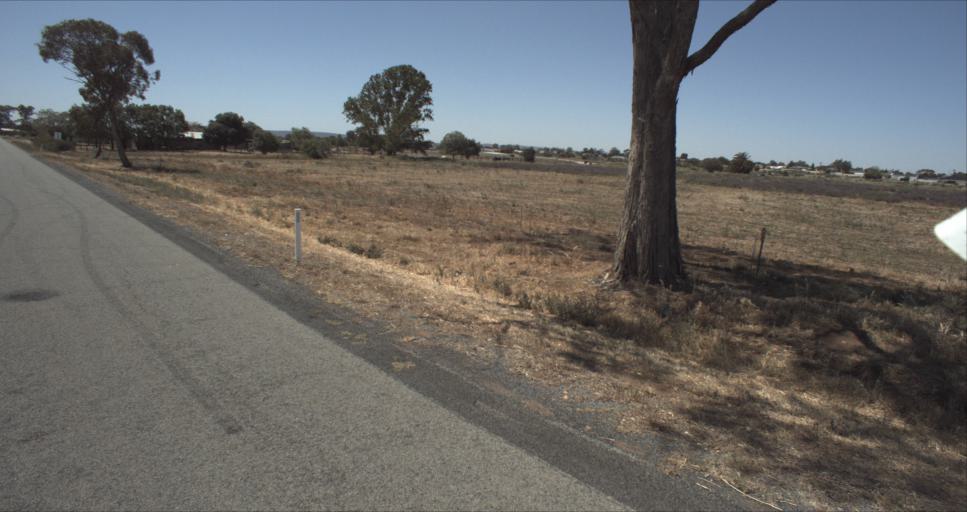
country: AU
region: New South Wales
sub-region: Leeton
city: Leeton
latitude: -34.5364
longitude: 146.3965
